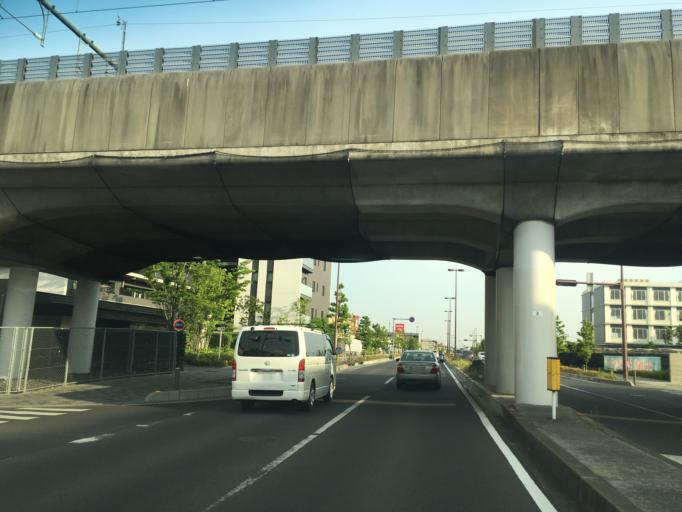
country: JP
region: Saitama
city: Yoshikawa
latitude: 35.8763
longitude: 139.8176
